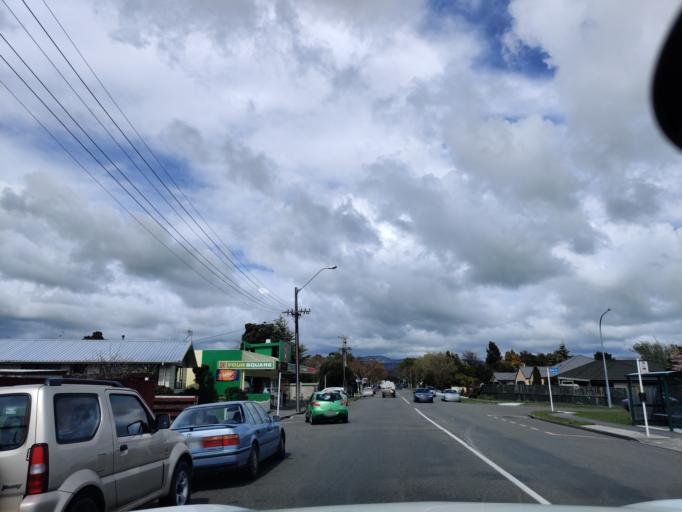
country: NZ
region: Manawatu-Wanganui
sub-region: Palmerston North City
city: Palmerston North
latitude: -40.3794
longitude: 175.5847
